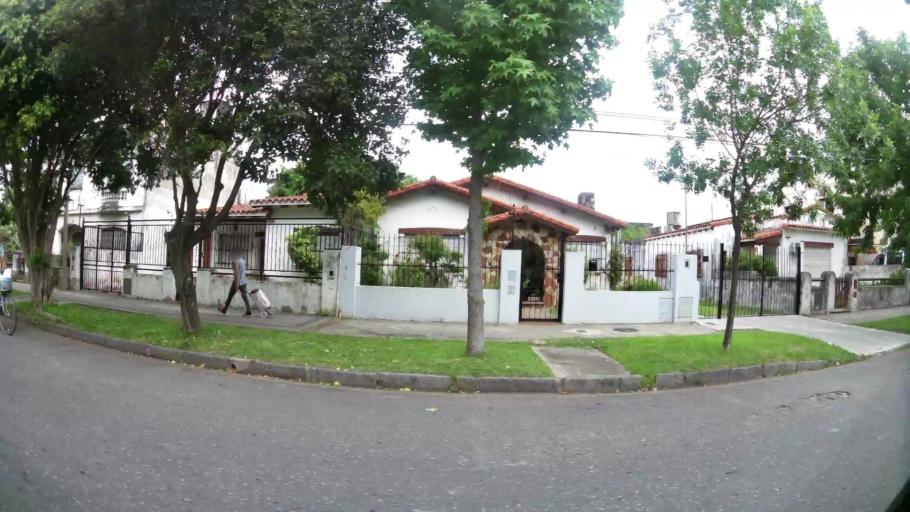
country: AR
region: Santa Fe
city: Gobernador Galvez
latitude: -32.9995
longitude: -60.6353
